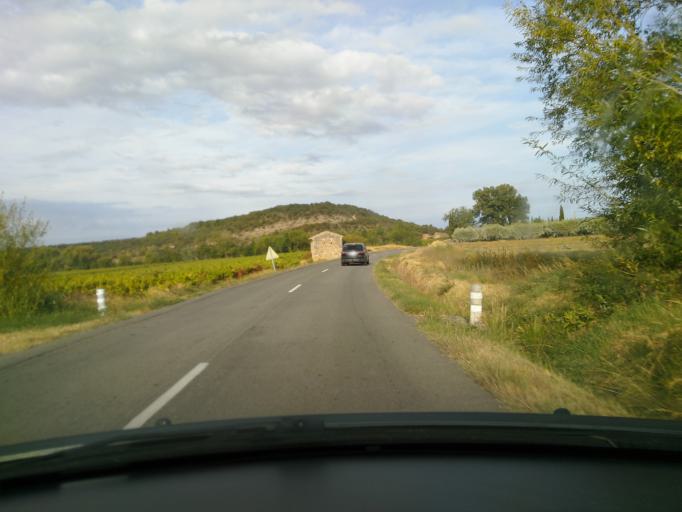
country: FR
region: Provence-Alpes-Cote d'Azur
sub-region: Departement du Vaucluse
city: Valreas
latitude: 44.4226
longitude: 5.0440
